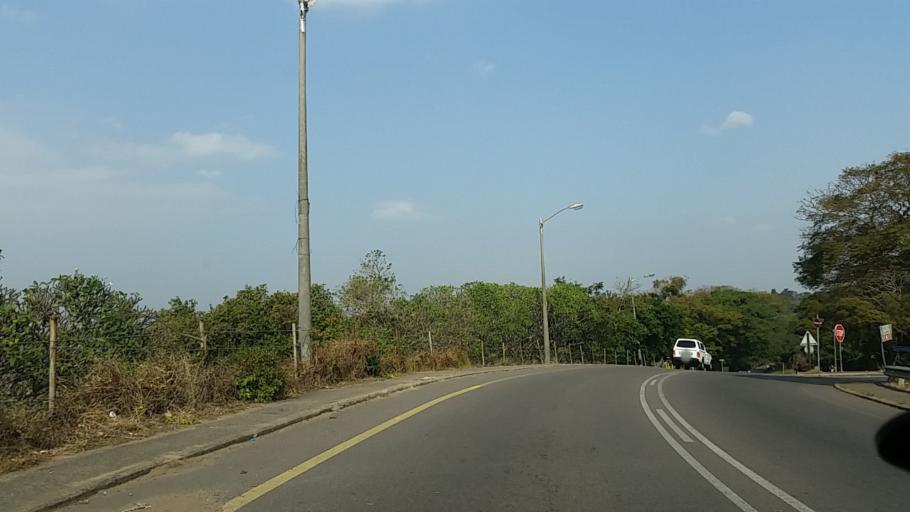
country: ZA
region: KwaZulu-Natal
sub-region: eThekwini Metropolitan Municipality
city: Berea
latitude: -29.8322
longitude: 30.9414
